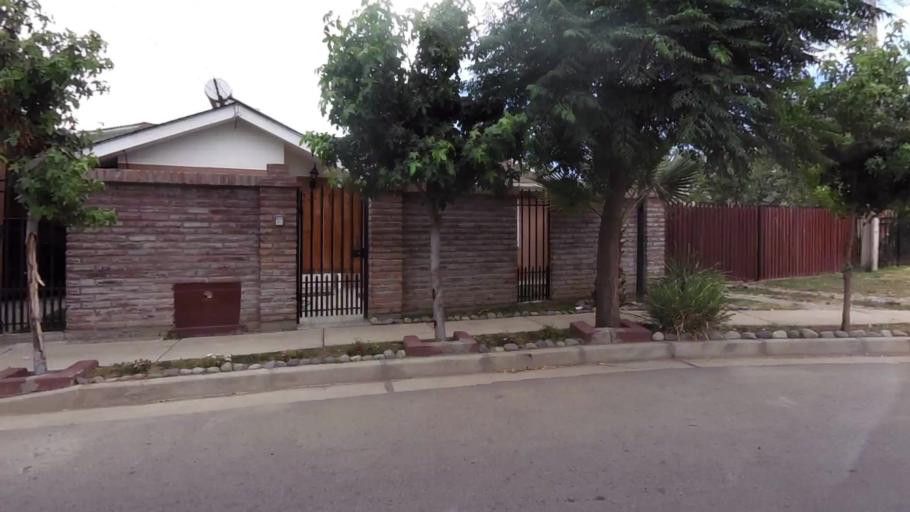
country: CL
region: O'Higgins
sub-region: Provincia de Cachapoal
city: Graneros
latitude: -34.0825
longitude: -70.7375
